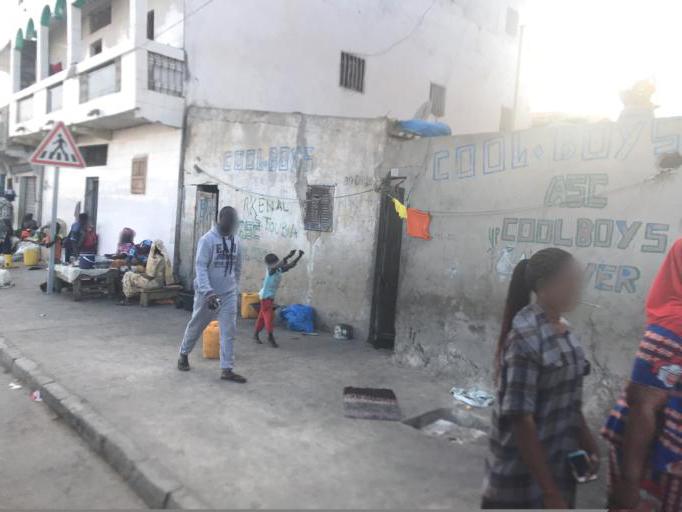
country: SN
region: Saint-Louis
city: Saint-Louis
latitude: 16.0246
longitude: -16.5073
